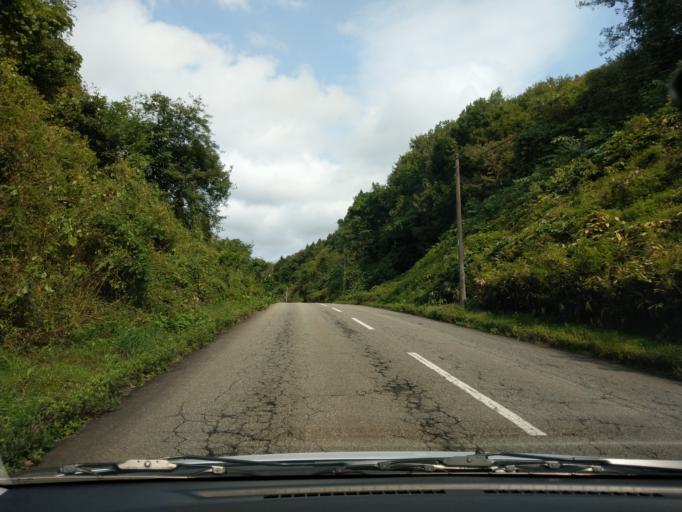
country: JP
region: Akita
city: Omagari
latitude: 39.4856
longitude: 140.3128
